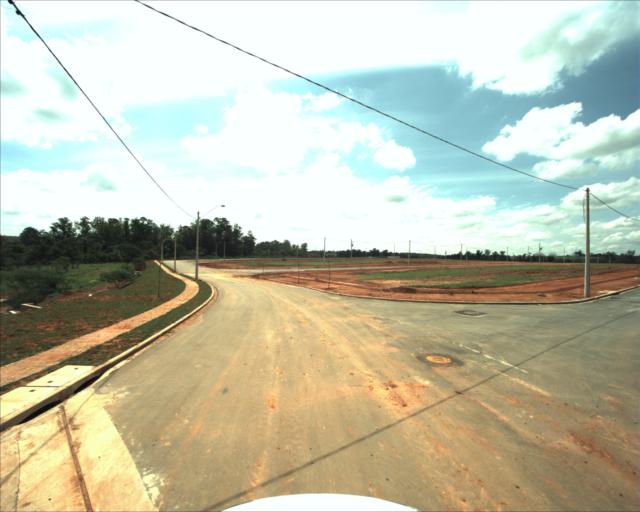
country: BR
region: Sao Paulo
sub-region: Sorocaba
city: Sorocaba
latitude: -23.4049
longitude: -47.4097
